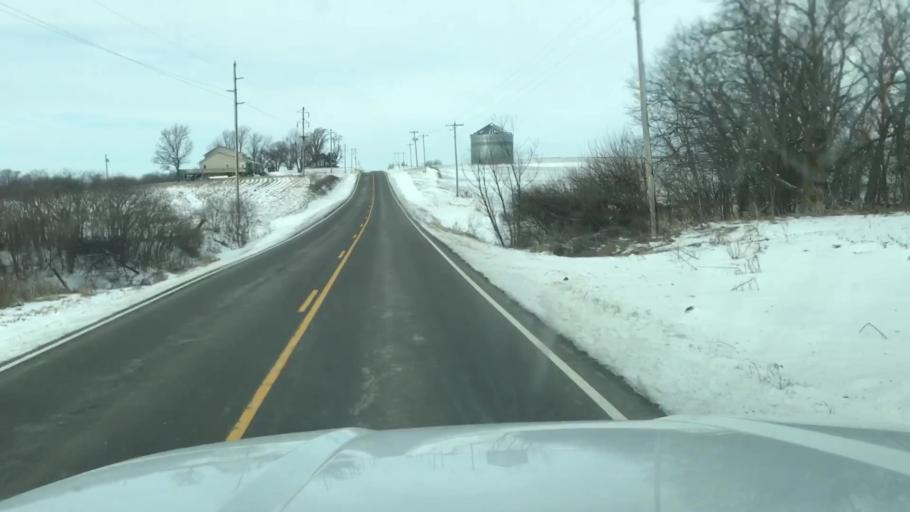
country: US
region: Missouri
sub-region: Holt County
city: Mound City
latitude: 40.1301
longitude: -95.1151
